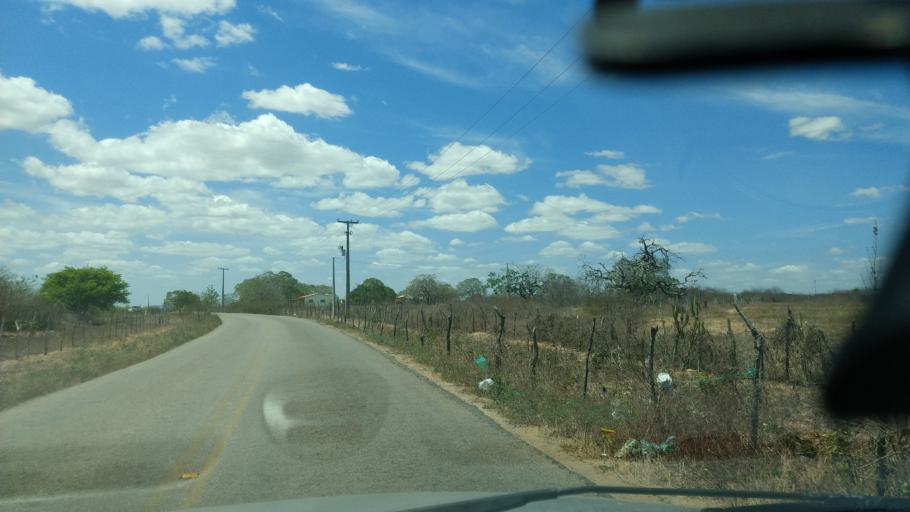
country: BR
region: Rio Grande do Norte
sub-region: Sao Paulo Do Potengi
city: Sao Paulo do Potengi
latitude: -5.9135
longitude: -35.7539
